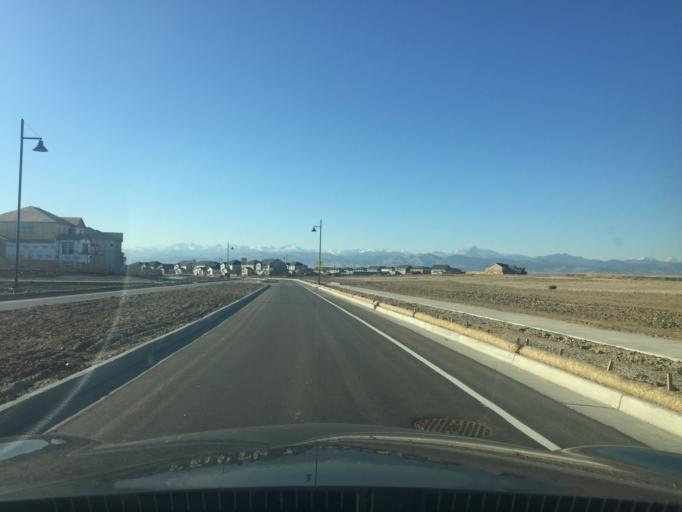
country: US
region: Colorado
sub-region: Boulder County
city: Erie
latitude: 40.0489
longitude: -105.0275
